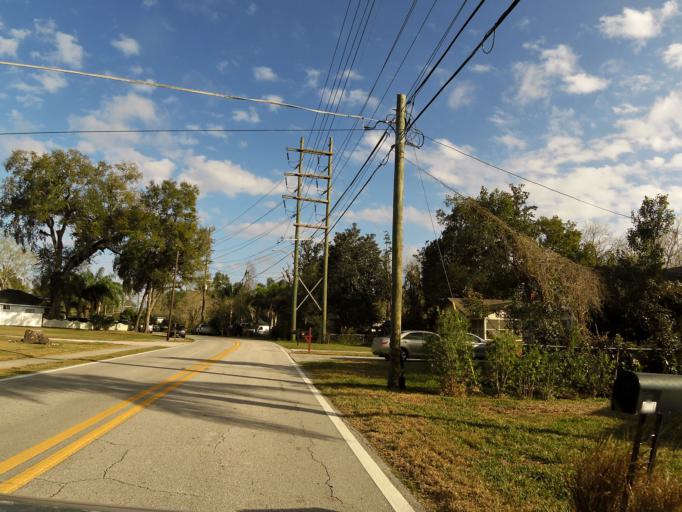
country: US
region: Florida
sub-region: Duval County
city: Jacksonville
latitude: 30.2866
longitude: -81.6167
